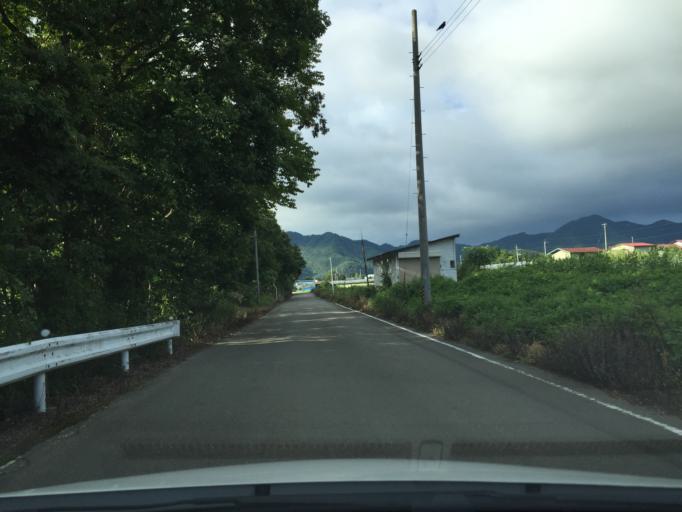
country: JP
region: Yamagata
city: Takahata
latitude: 37.9351
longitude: 140.2031
